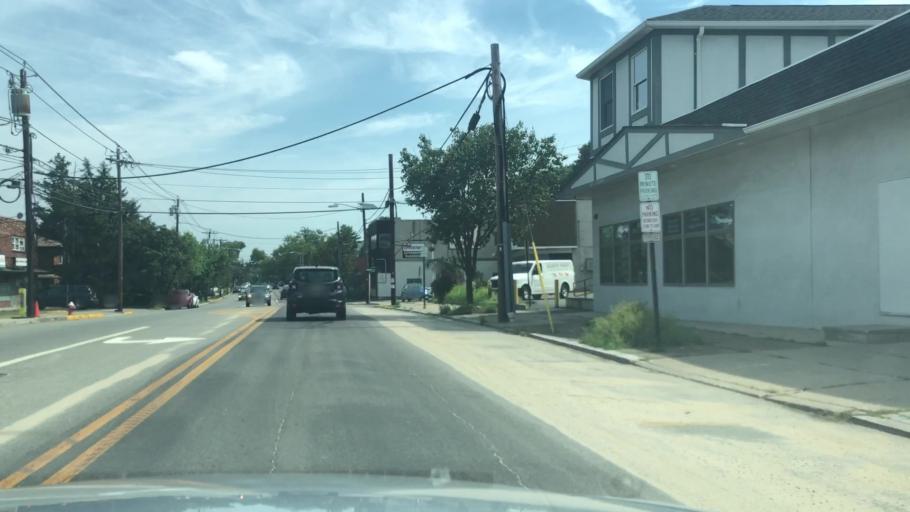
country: US
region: New Jersey
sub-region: Bergen County
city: Cliffside Park
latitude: 40.8292
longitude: -73.9938
